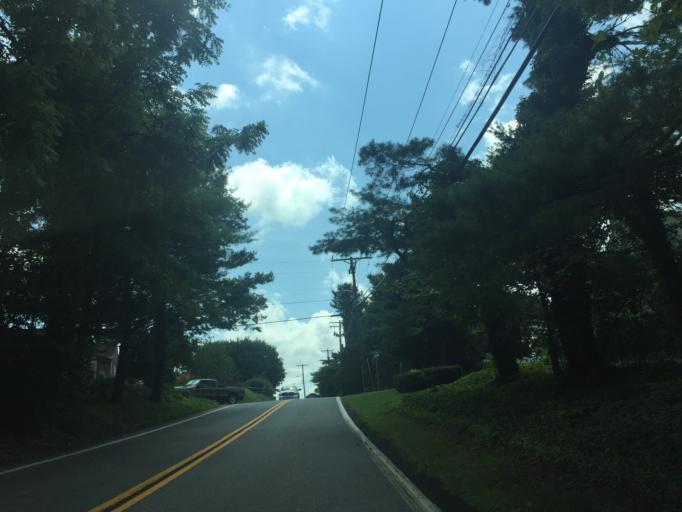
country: US
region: Maryland
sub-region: Baltimore County
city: Kingsville
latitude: 39.4444
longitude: -76.4156
